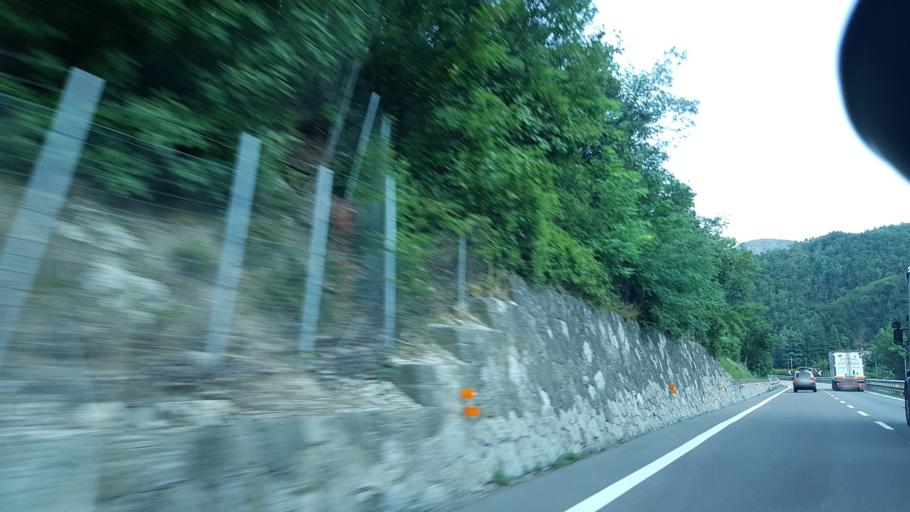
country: IT
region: Liguria
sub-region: Provincia di Genova
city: Isola del Cantone
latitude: 44.6534
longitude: 8.9481
